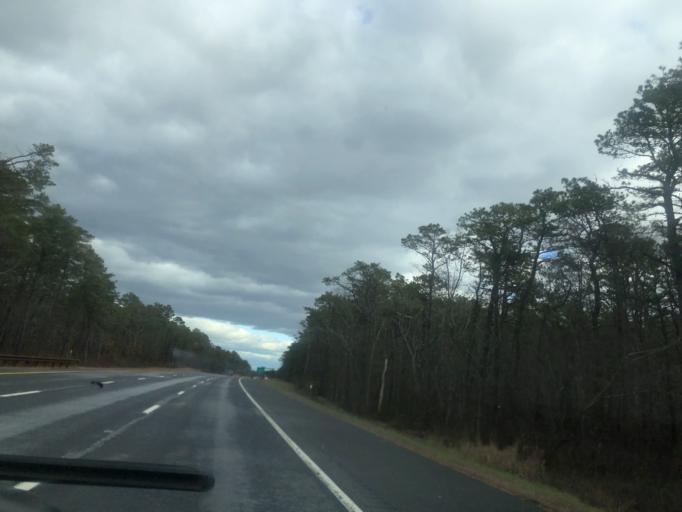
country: US
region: New Jersey
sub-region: Ocean County
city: Tuckerton
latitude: 39.6326
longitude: -74.3811
